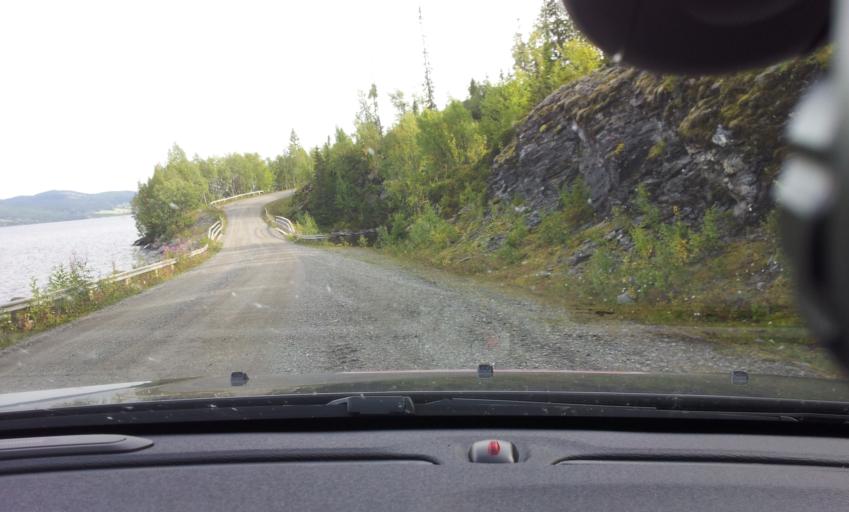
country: SE
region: Jaemtland
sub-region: Are Kommun
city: Are
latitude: 63.5830
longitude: 12.9185
